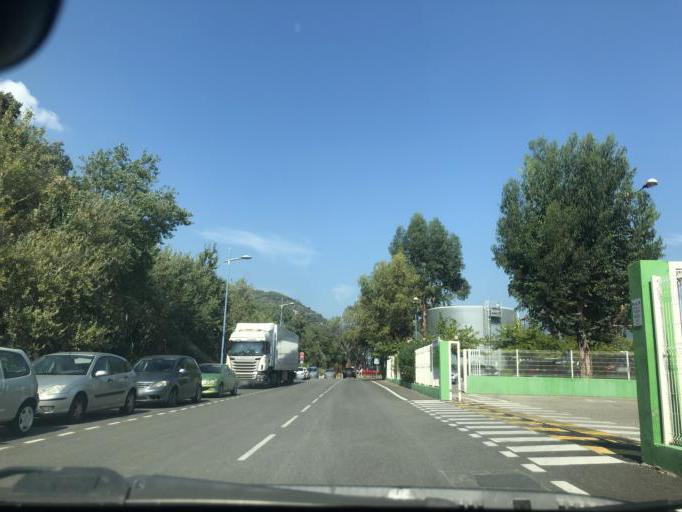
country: FR
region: Provence-Alpes-Cote d'Azur
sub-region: Departement des Alpes-Maritimes
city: Carros
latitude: 43.7880
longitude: 7.2081
